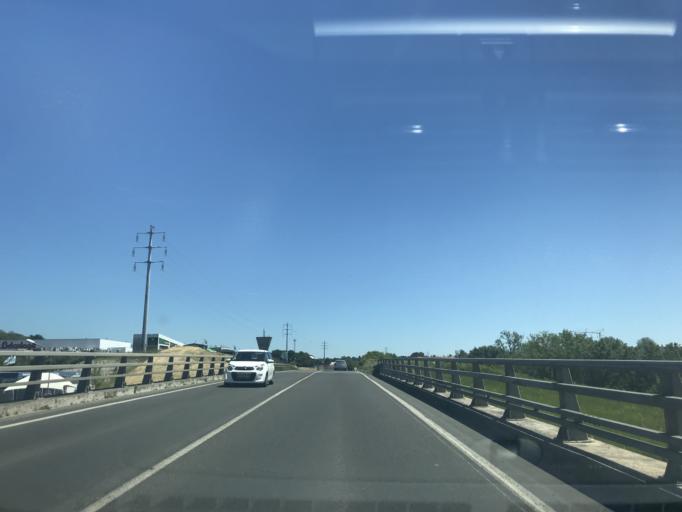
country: FR
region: Poitou-Charentes
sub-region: Departement de la Charente-Maritime
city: Royan
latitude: 45.6308
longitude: -1.0066
